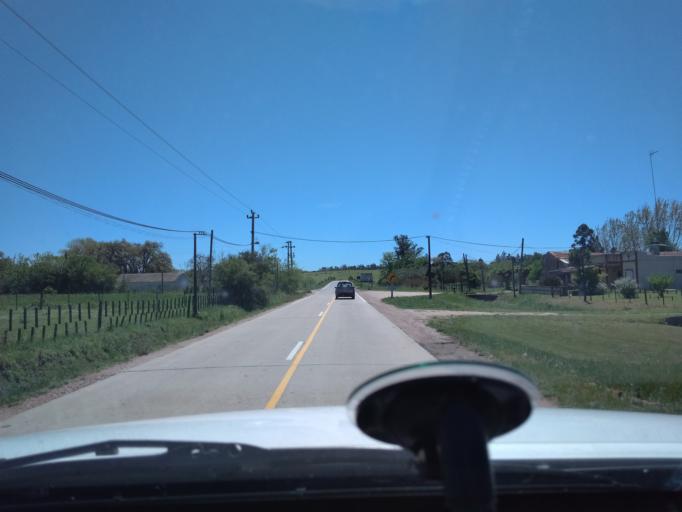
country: UY
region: Canelones
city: Las Piedras
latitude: -34.7207
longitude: -56.2899
